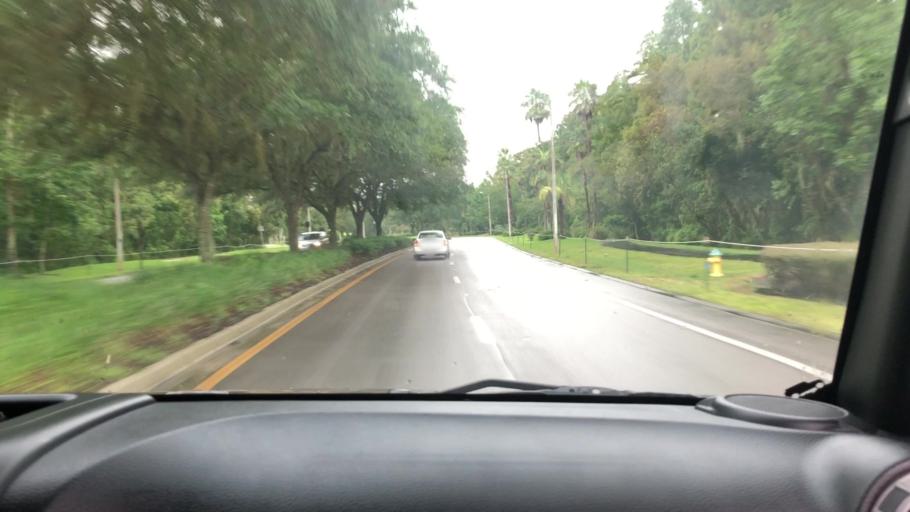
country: US
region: Florida
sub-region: Hillsborough County
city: Pebble Creek
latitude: 28.1150
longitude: -82.3905
